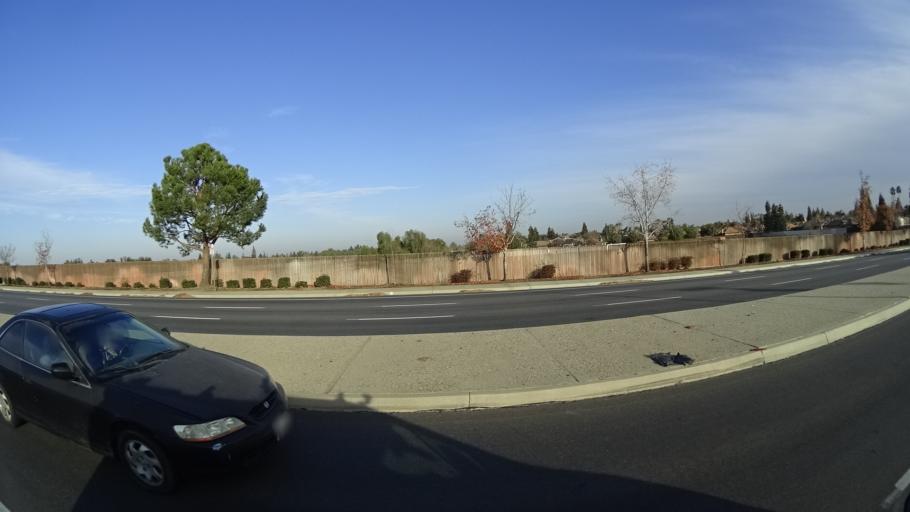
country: US
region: California
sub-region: Kern County
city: Greenacres
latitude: 35.3985
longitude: -119.1013
